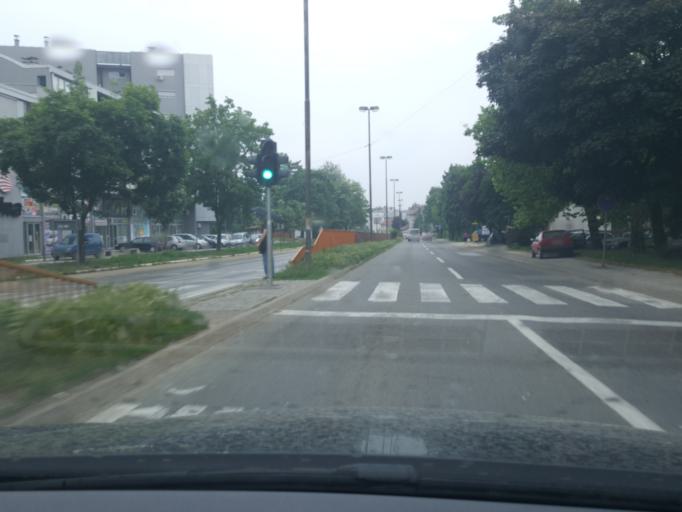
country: RS
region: Central Serbia
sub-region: Kolubarski Okrug
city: Valjevo
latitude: 44.2740
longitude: 19.8922
